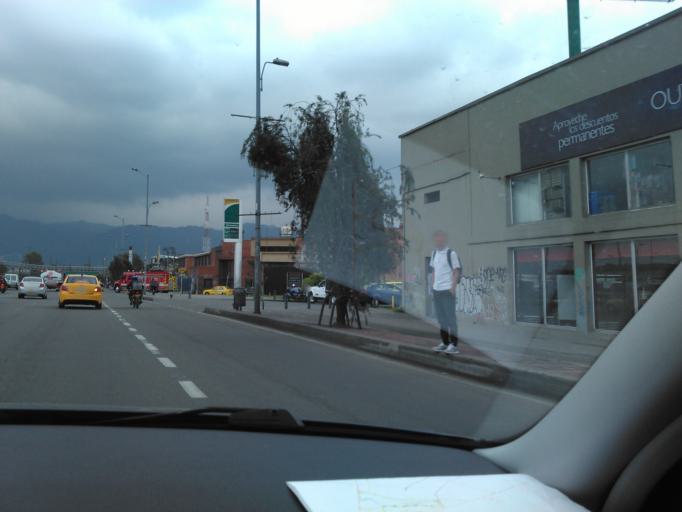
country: CO
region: Bogota D.C.
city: Bogota
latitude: 4.6277
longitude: -74.1126
